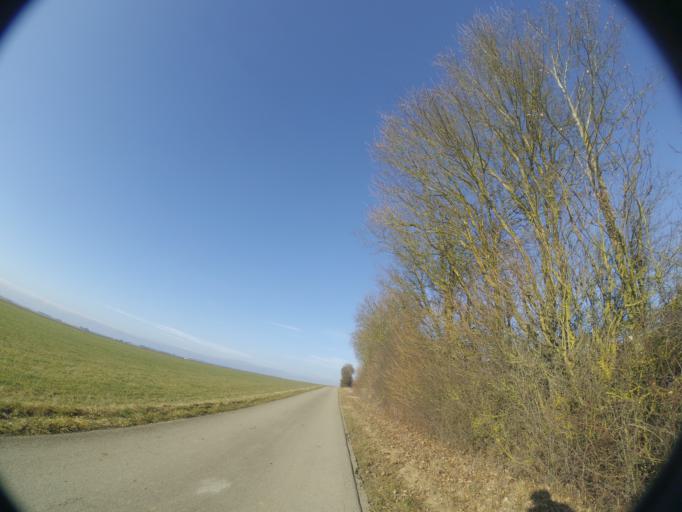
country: DE
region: Baden-Wuerttemberg
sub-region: Tuebingen Region
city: Dornstadt
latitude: 48.4760
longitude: 9.9376
